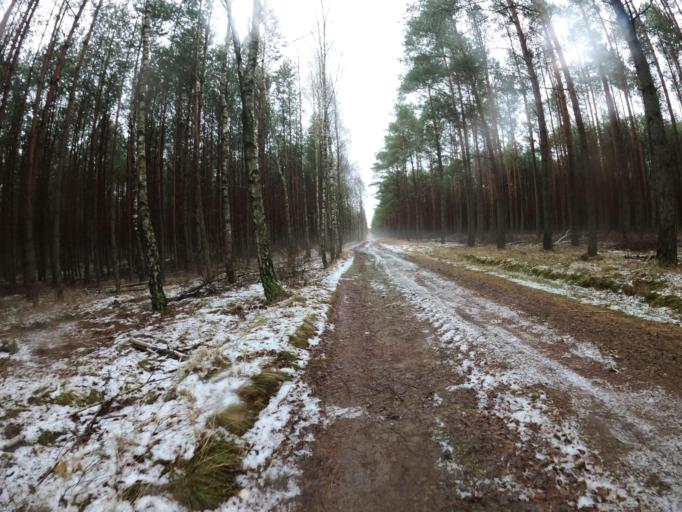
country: PL
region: Lubusz
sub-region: Powiat slubicki
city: Cybinka
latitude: 52.1998
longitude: 14.9230
